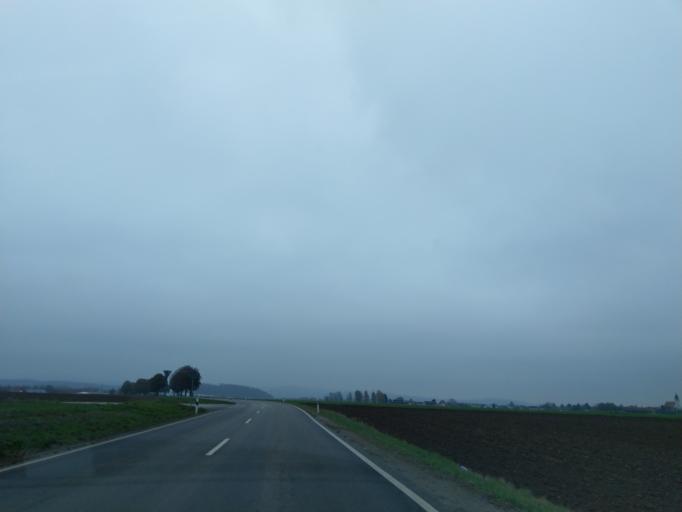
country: DE
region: Bavaria
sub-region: Lower Bavaria
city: Plattling
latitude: 48.8142
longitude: 12.8751
